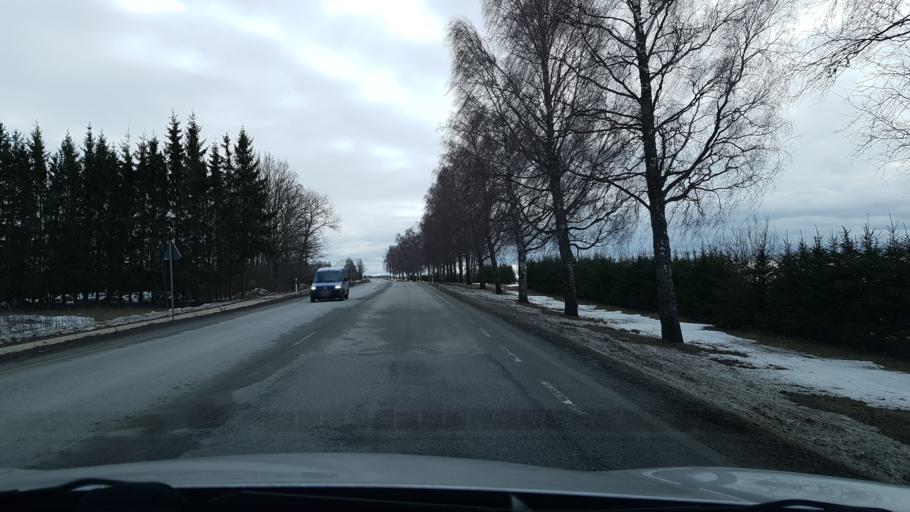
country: EE
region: Jogevamaa
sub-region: Jogeva linn
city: Jogeva
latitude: 58.7349
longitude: 26.3761
